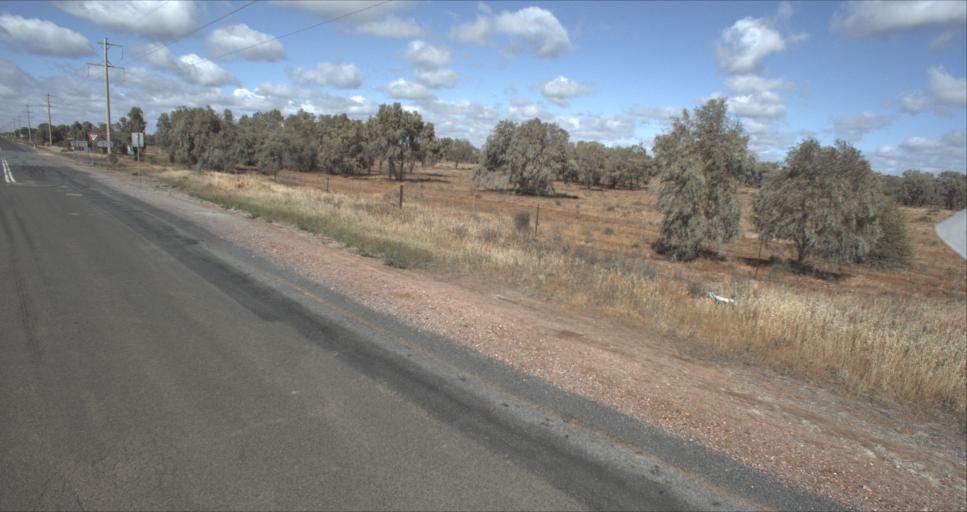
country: AU
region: New South Wales
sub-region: Murrumbidgee Shire
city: Darlington Point
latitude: -34.5162
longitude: 146.1766
